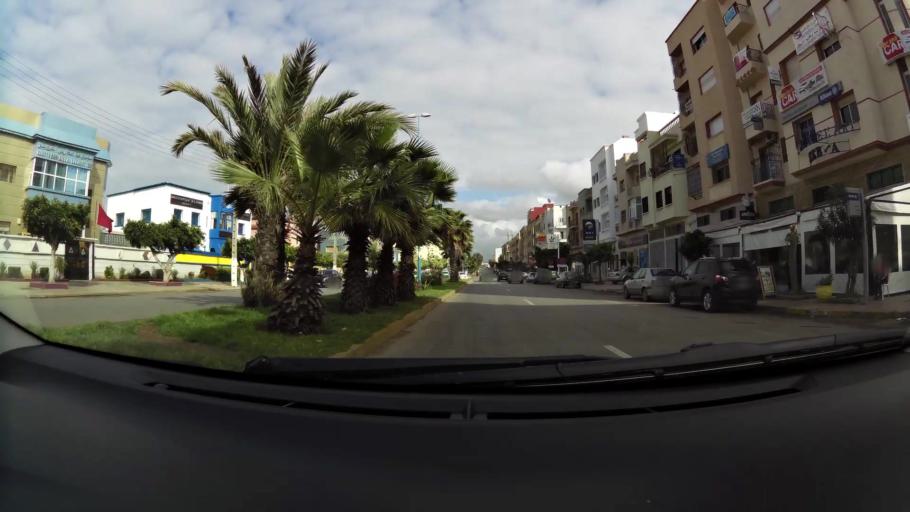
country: MA
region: Grand Casablanca
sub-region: Mohammedia
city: Mohammedia
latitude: 33.6945
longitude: -7.3796
